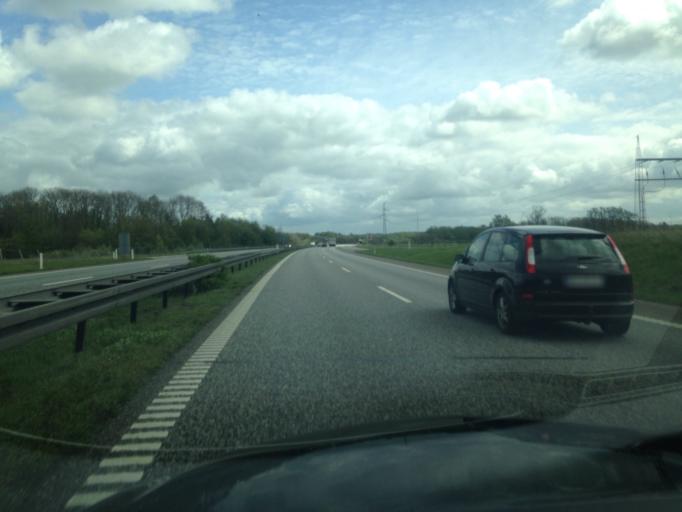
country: DK
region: South Denmark
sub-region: Kerteminde Kommune
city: Langeskov
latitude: 55.3655
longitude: 10.5193
